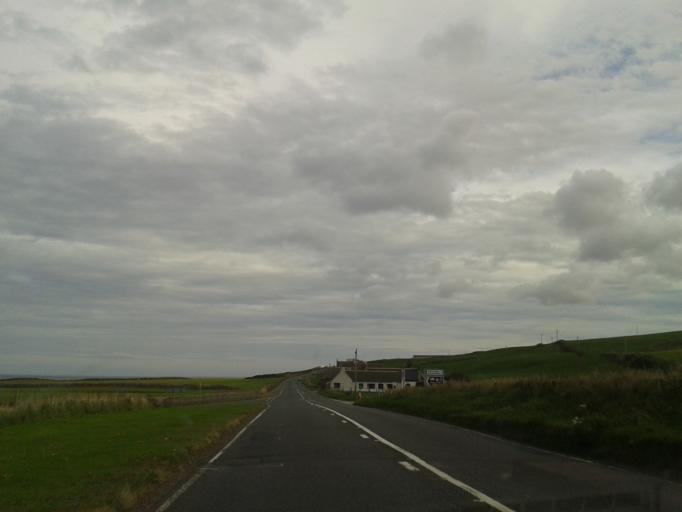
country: GB
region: Scotland
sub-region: Aberdeenshire
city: Banff
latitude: 57.6664
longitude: -2.5540
